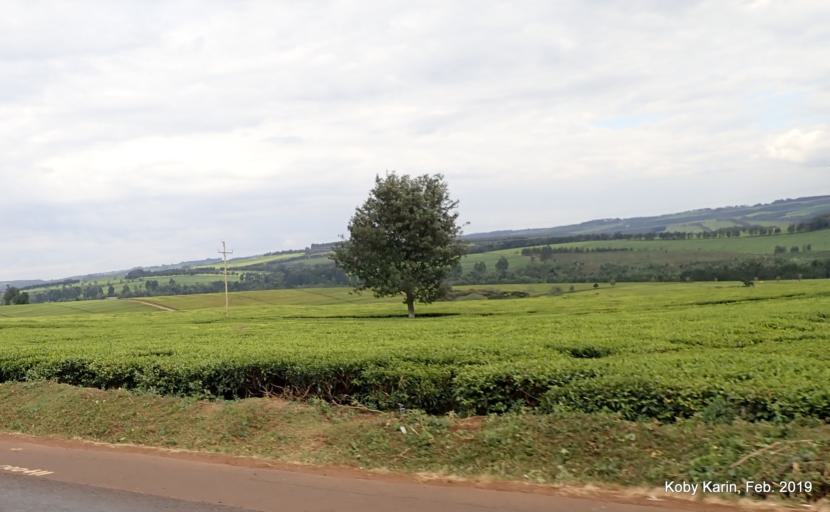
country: KE
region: Kericho
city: Litein
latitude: -0.4632
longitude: 35.1818
